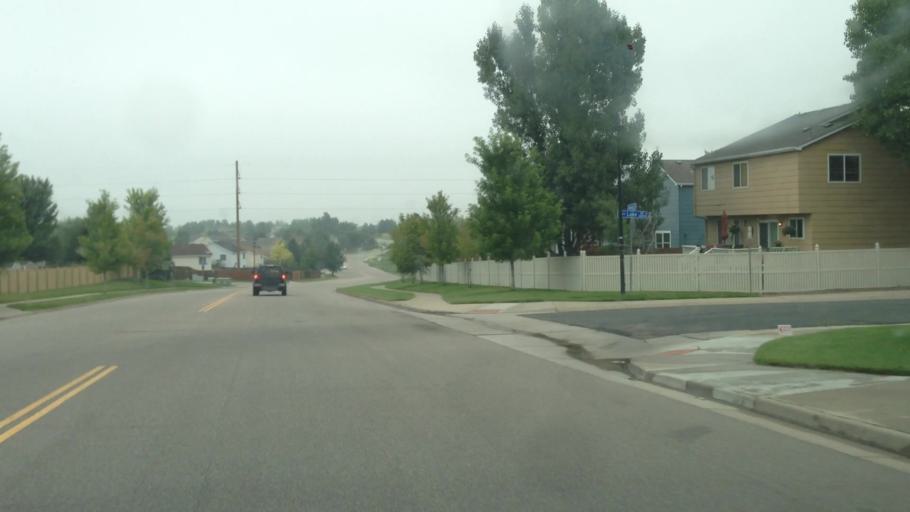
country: US
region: Colorado
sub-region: Douglas County
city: Parker
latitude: 39.6080
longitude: -104.7302
